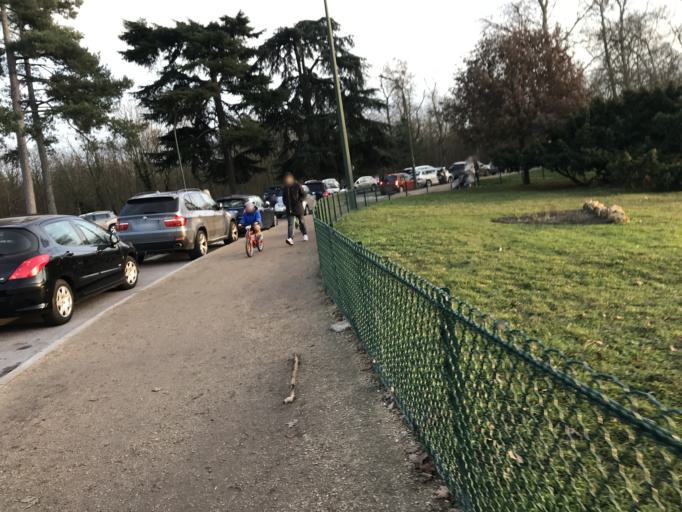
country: FR
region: Ile-de-France
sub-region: Departement des Hauts-de-Seine
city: Neuilly-sur-Seine
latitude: 48.8682
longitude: 2.2653
